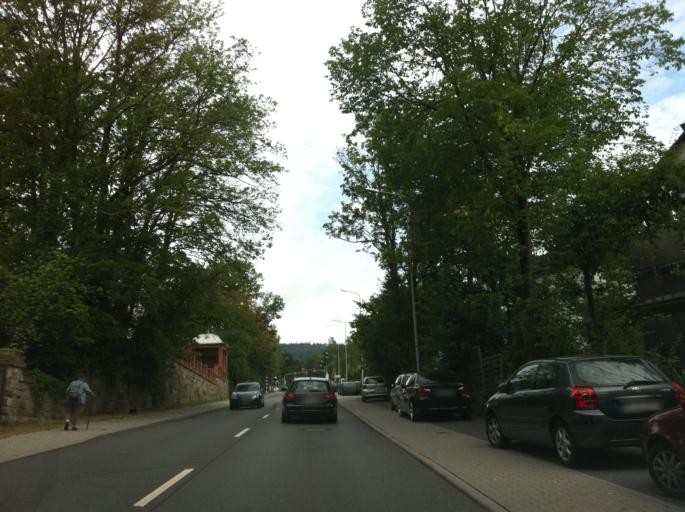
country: DE
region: Hesse
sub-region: Regierungsbezirk Darmstadt
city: Konigstein im Taunus
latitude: 50.1903
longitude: 8.4651
